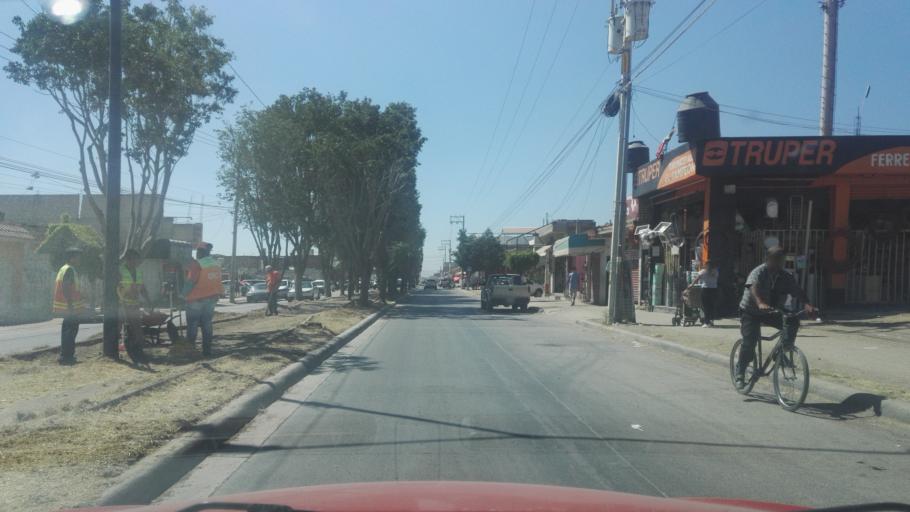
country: MX
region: Guanajuato
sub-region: Leon
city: Fraccionamiento Paraiso Real
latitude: 21.0967
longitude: -101.5898
